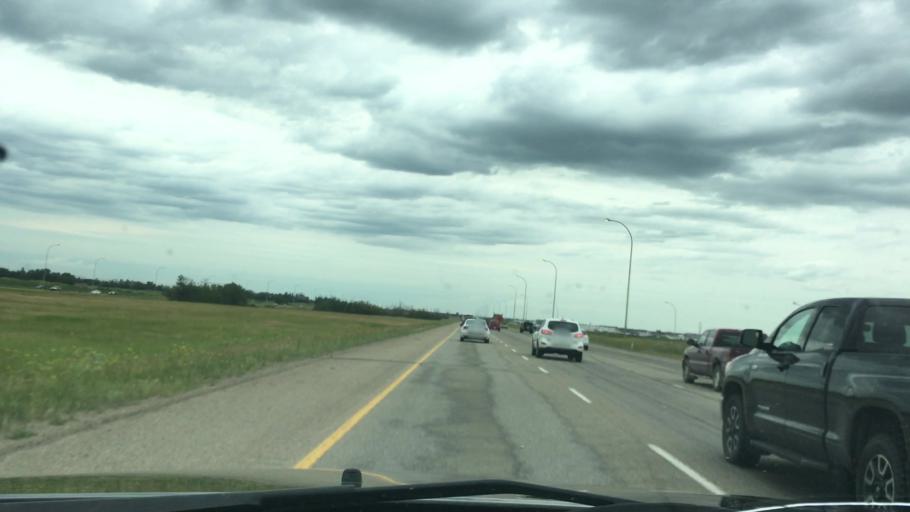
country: CA
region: Alberta
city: Leduc
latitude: 53.3106
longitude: -113.5480
